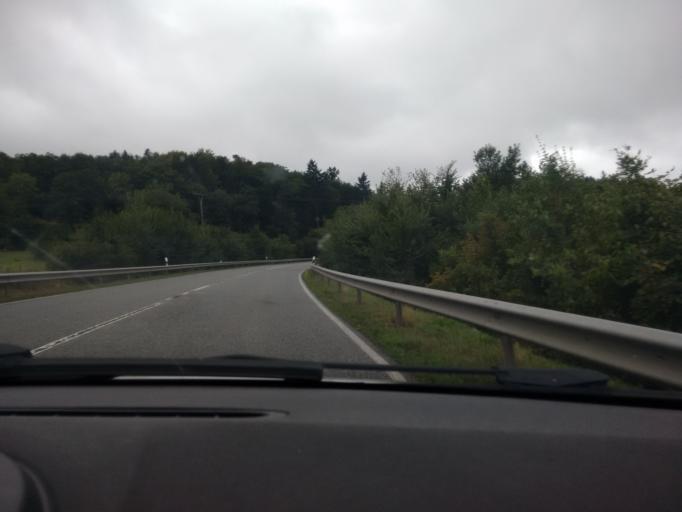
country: DE
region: Rheinland-Pfalz
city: Schmissberg
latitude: 49.6578
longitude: 7.1903
